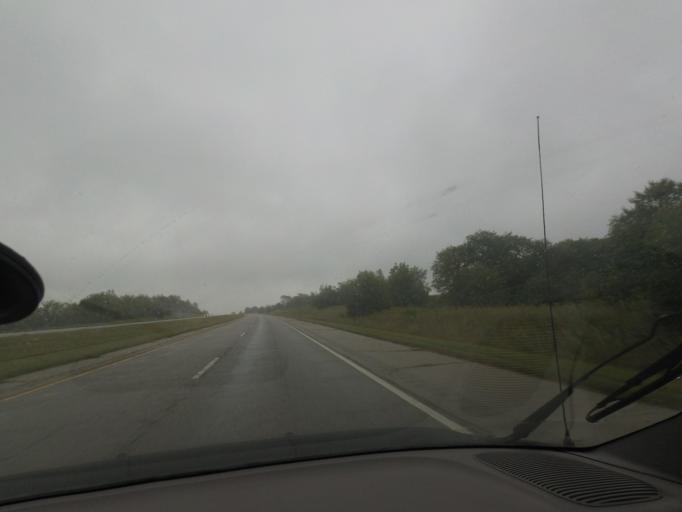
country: US
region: Illinois
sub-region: Pike County
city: Barry
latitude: 39.6926
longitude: -90.9957
